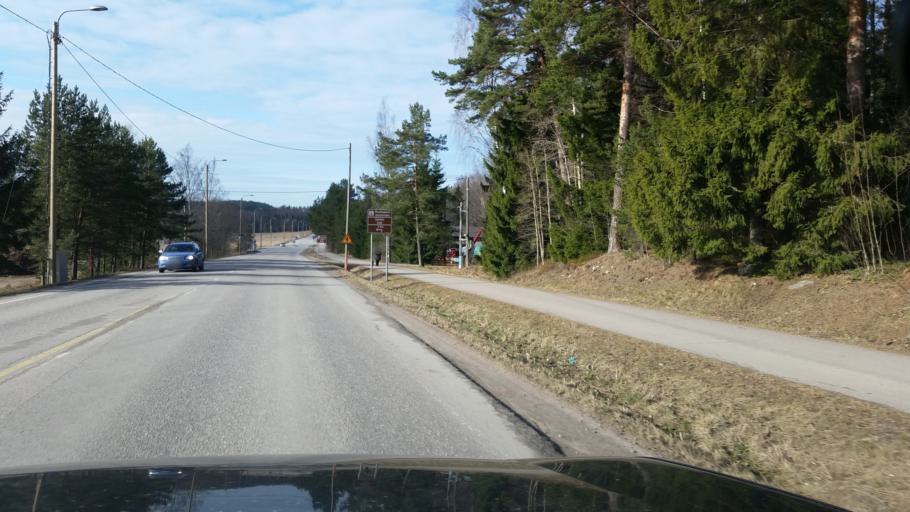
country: FI
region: Uusimaa
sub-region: Helsinki
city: Kirkkonummi
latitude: 60.1082
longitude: 24.4417
